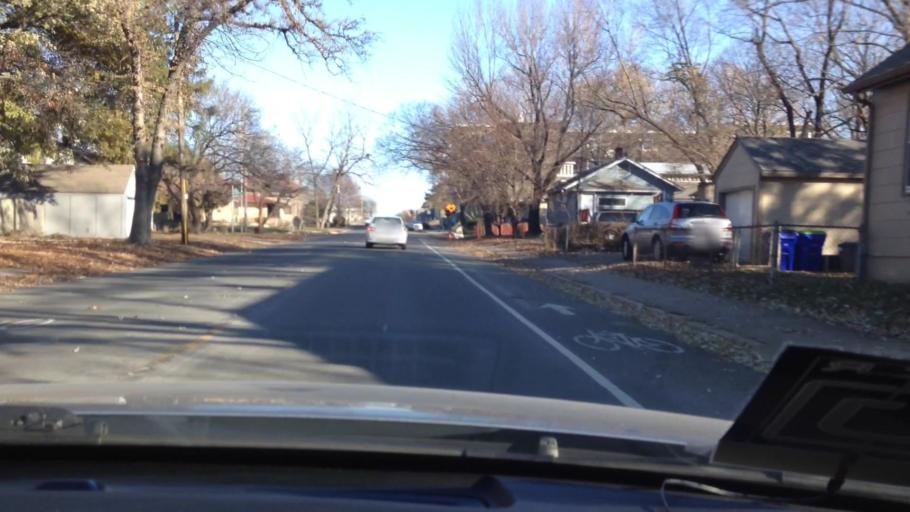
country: US
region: Kansas
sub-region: Johnson County
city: Overland Park
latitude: 38.9858
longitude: -94.6757
